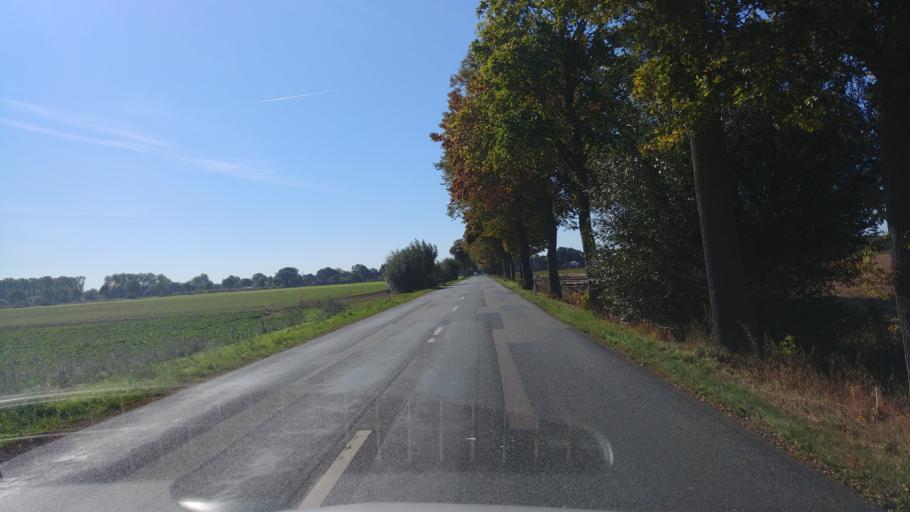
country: DE
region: Lower Saxony
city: Meinersen
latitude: 52.4943
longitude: 10.3460
